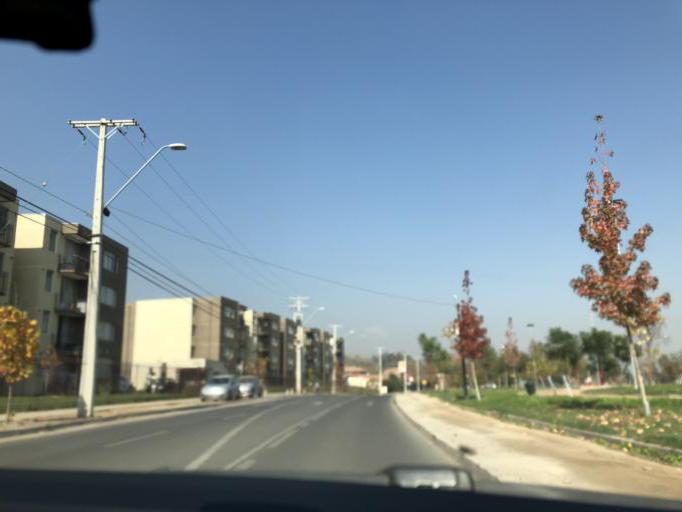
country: CL
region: Santiago Metropolitan
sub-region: Provincia de Cordillera
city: Puente Alto
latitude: -33.5669
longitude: -70.5515
